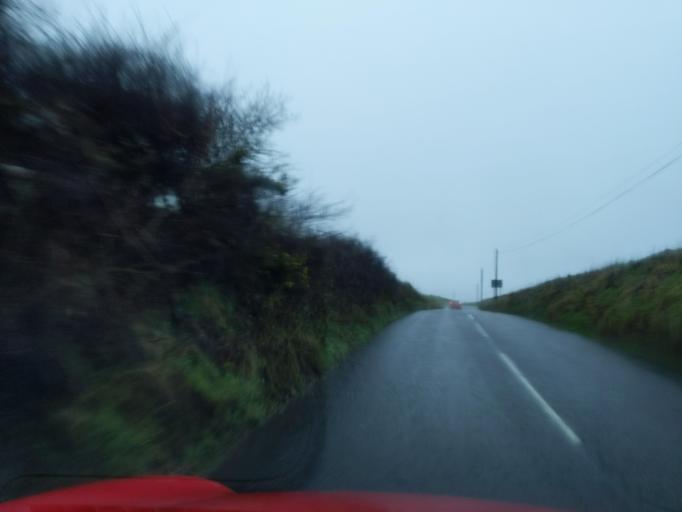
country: GB
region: England
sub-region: Cornwall
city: Camelford
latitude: 50.6405
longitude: -4.6943
